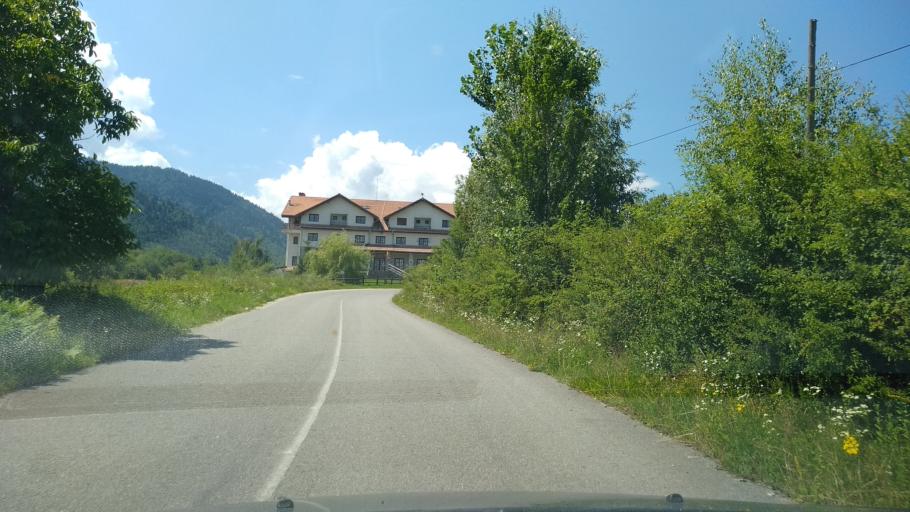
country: RO
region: Hunedoara
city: Salasu de Sus
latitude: 45.4847
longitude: 22.9352
